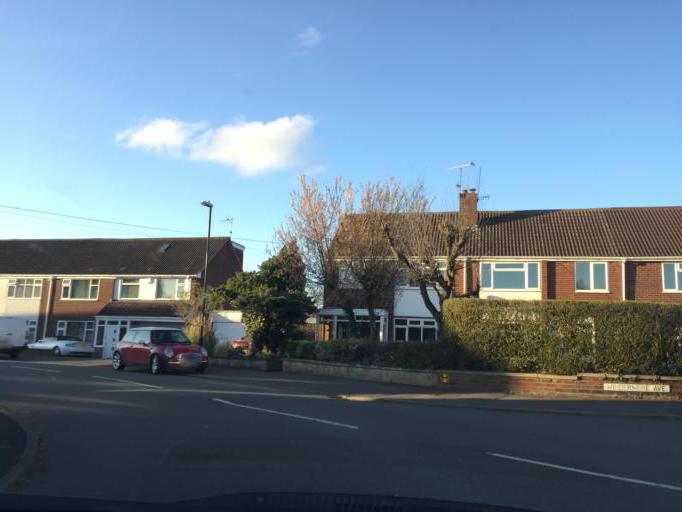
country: GB
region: England
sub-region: Warwickshire
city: Ryton on Dunsmore
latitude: 52.4015
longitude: -1.4514
